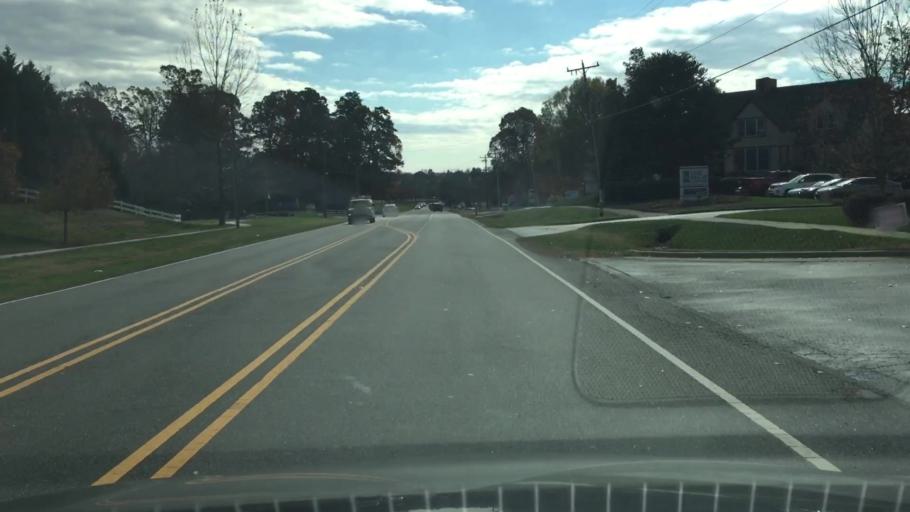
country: US
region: North Carolina
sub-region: Iredell County
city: Mooresville
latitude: 35.5728
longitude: -80.8684
